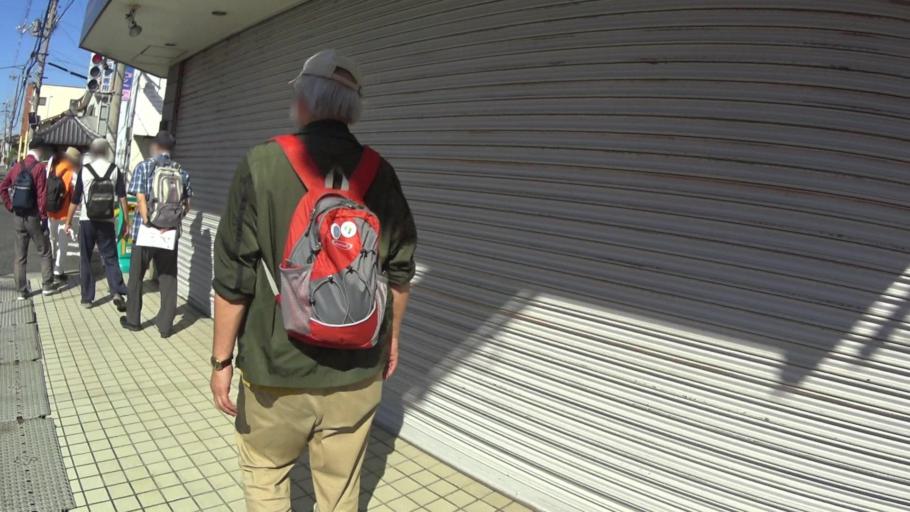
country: JP
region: Mie
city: Ise
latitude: 34.5341
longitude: 136.5994
